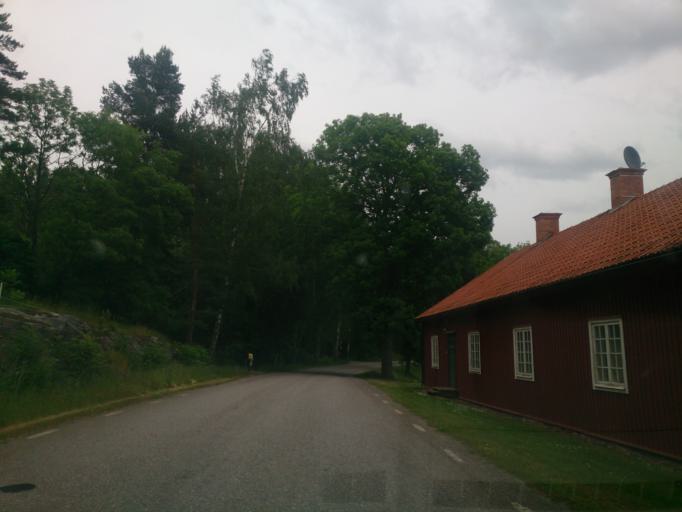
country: SE
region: OEstergoetland
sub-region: Soderkopings Kommun
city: Soederkoeping
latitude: 58.3021
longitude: 16.2591
